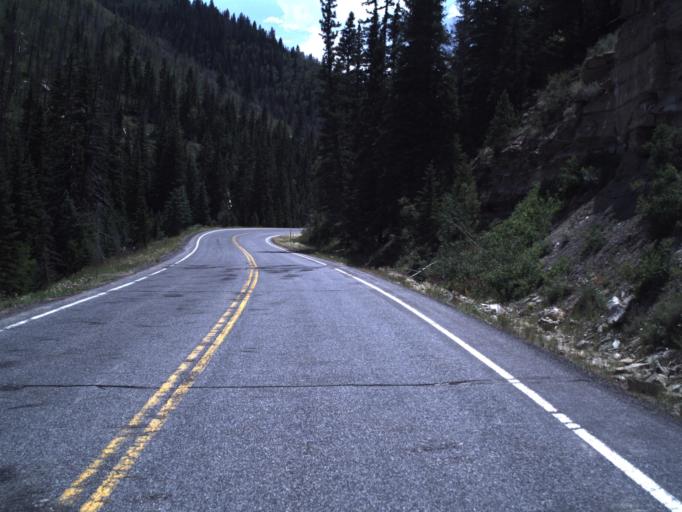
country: US
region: Utah
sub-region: Emery County
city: Huntington
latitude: 39.5076
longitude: -111.1566
